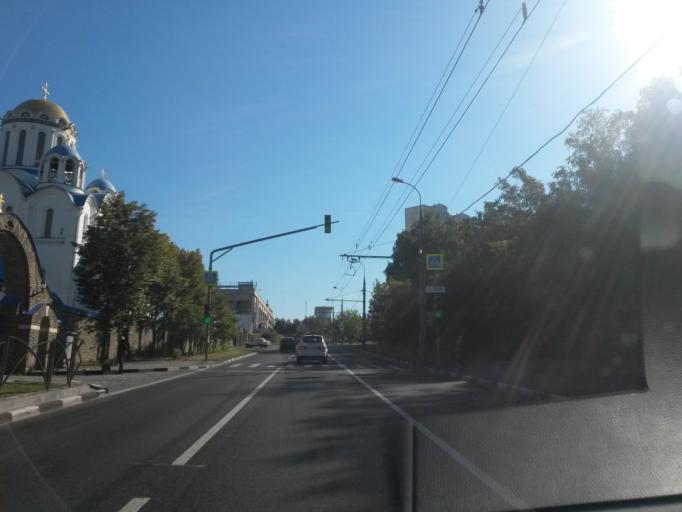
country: RU
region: Moscow
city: Yasenevo
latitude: 55.6162
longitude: 37.5398
